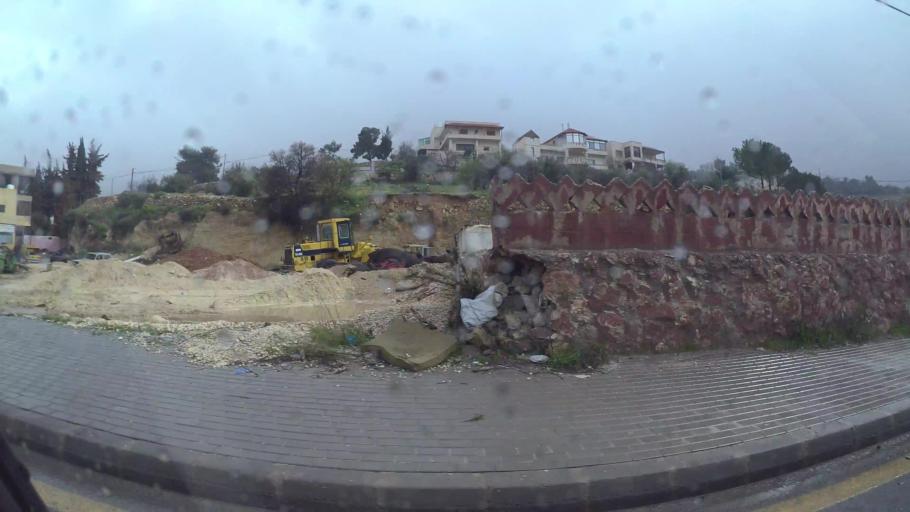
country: JO
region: Amman
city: Wadi as Sir
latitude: 32.0101
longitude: 35.7927
